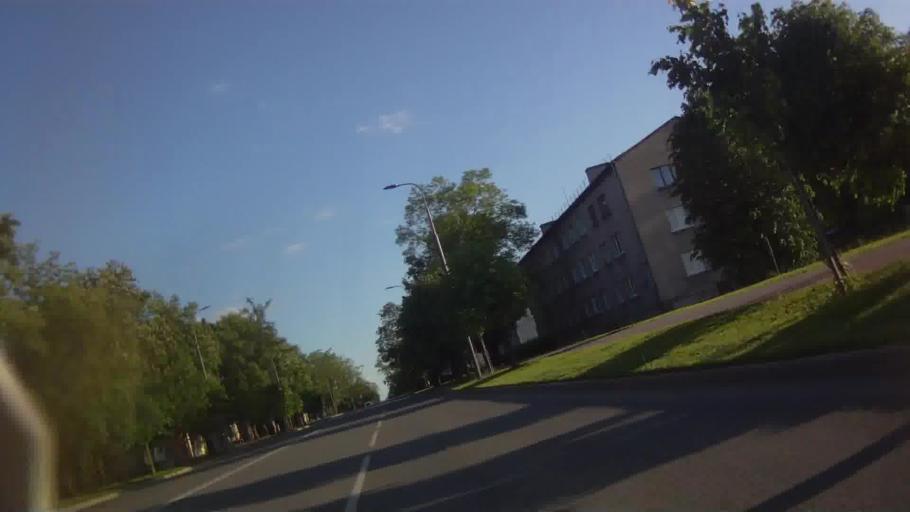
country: LV
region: Rezekne
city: Rezekne
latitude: 56.5124
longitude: 27.3343
